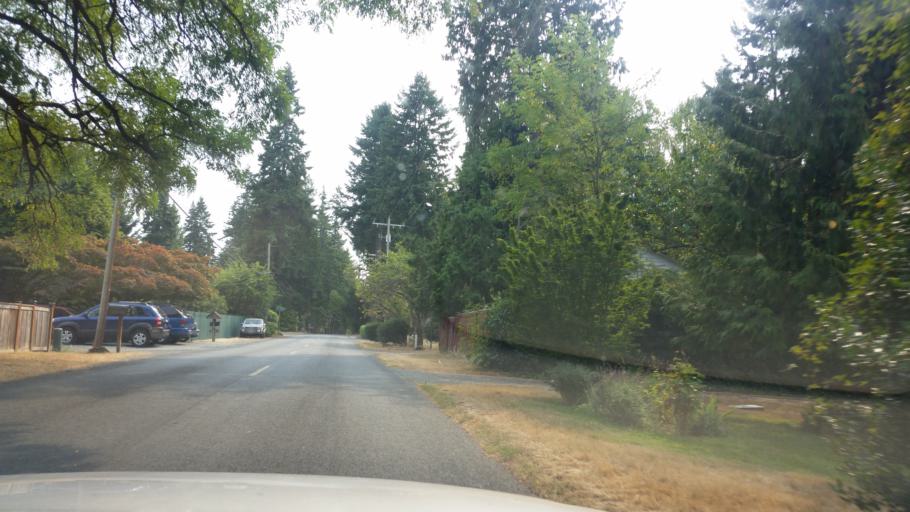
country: US
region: Washington
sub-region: Snohomish County
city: Meadowdale
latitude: 47.8388
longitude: -122.3304
